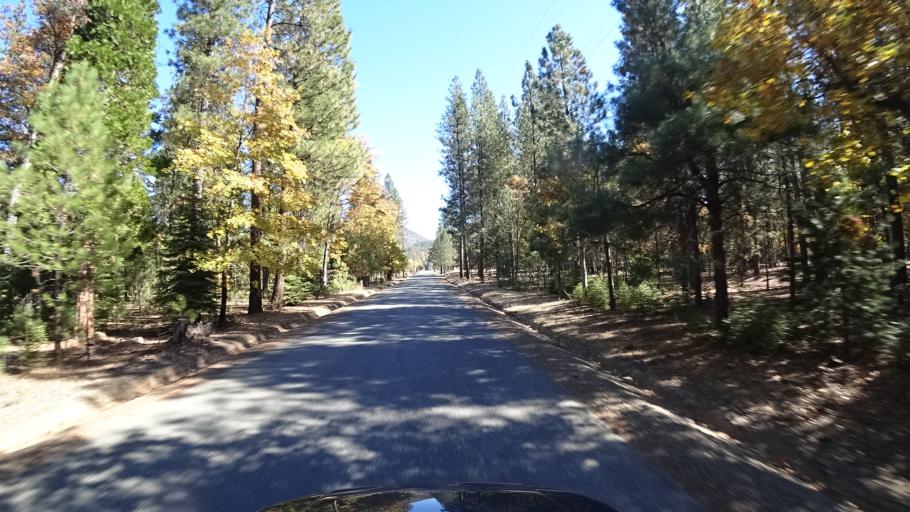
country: US
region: California
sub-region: Siskiyou County
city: Yreka
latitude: 41.5816
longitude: -122.9710
